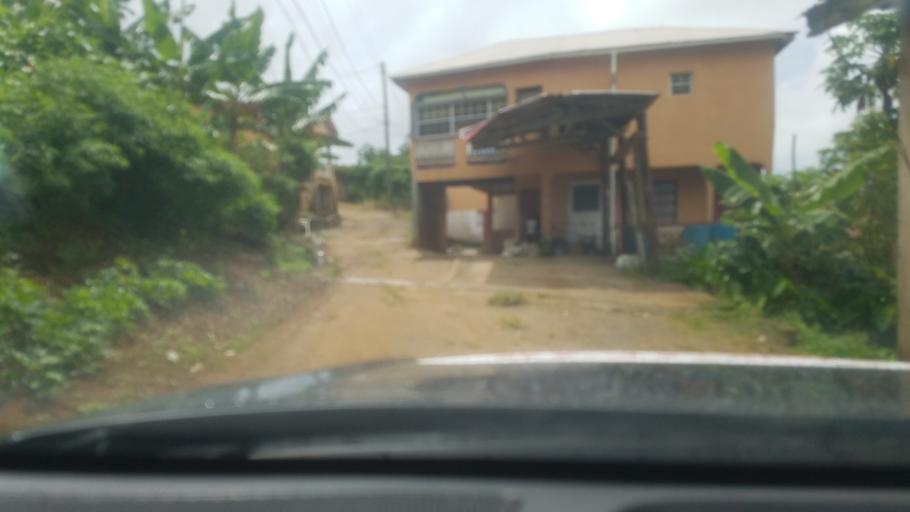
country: LC
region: Micoud Quarter
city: Micoud
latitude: 13.8074
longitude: -60.9477
